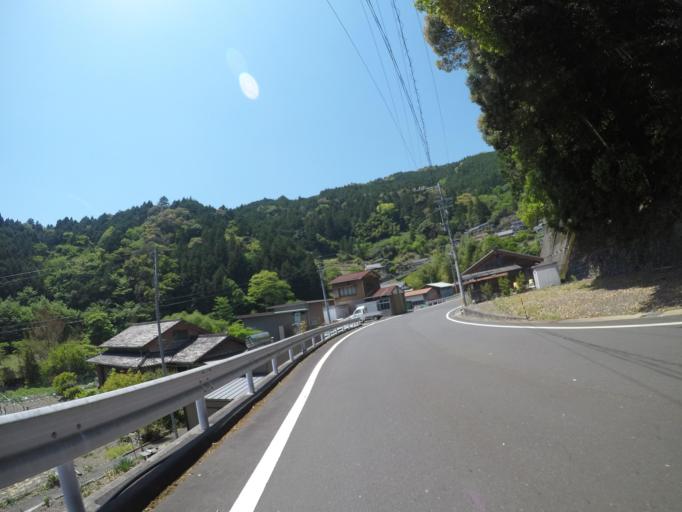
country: JP
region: Shizuoka
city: Shizuoka-shi
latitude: 35.1025
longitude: 138.2296
